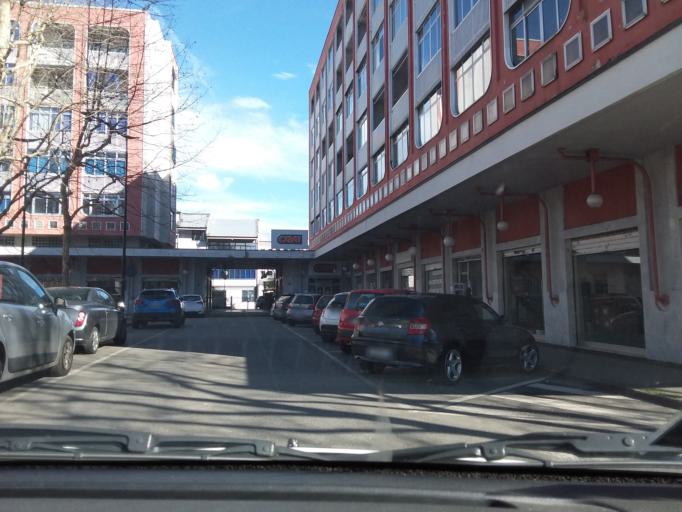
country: IT
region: Piedmont
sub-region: Provincia di Torino
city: Collegno
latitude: 45.0753
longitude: 7.5548
